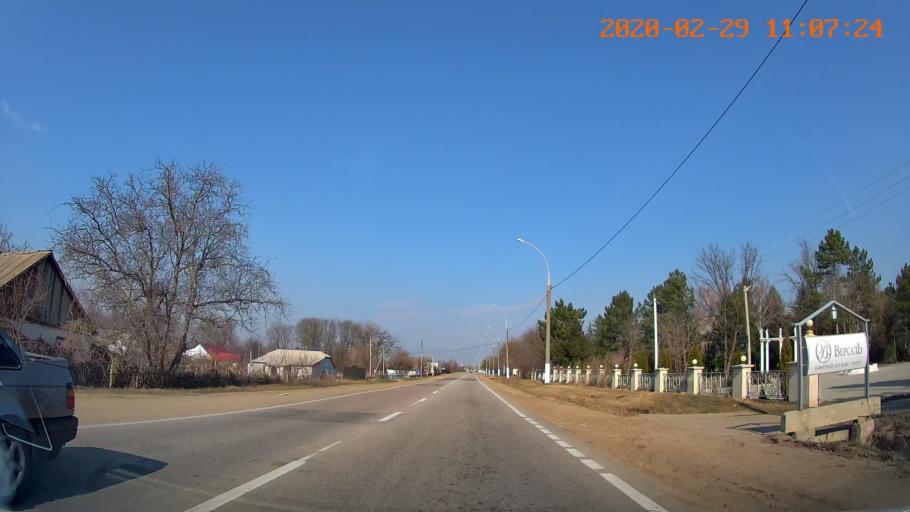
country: MD
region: Criuleni
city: Criuleni
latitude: 47.2250
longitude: 29.1823
